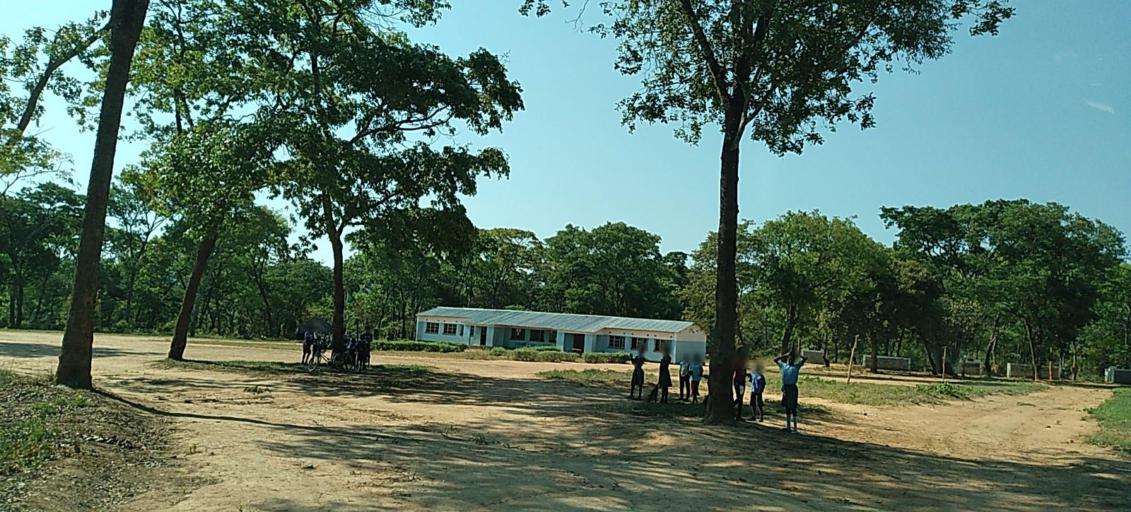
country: ZM
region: Central
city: Mkushi
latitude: -13.4742
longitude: 28.9809
